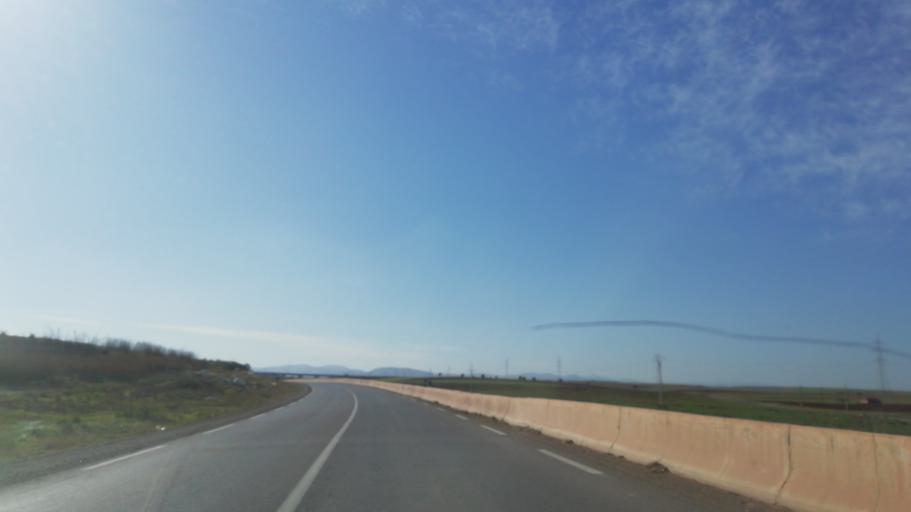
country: DZ
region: Tlemcen
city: Ouled Mimoun
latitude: 35.0175
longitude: -0.9042
